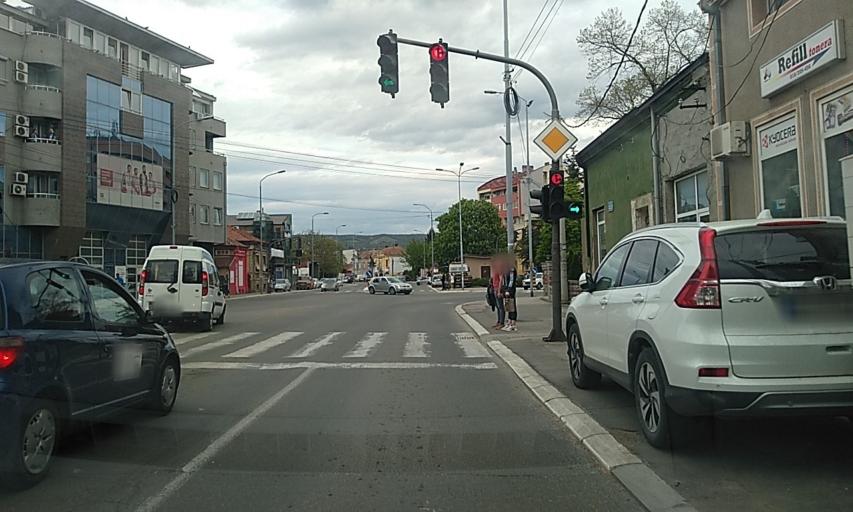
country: RS
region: Central Serbia
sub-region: Nisavski Okrug
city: Nis
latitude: 43.3234
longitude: 21.9022
